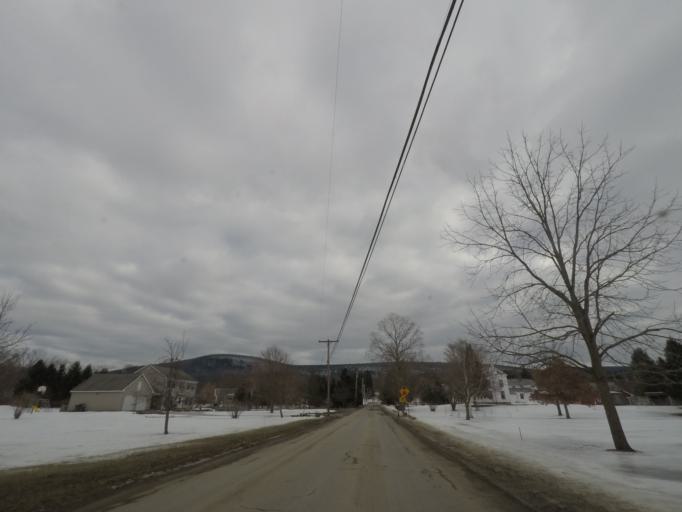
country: US
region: New York
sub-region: Rensselaer County
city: Poestenkill
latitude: 42.7366
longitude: -73.5654
